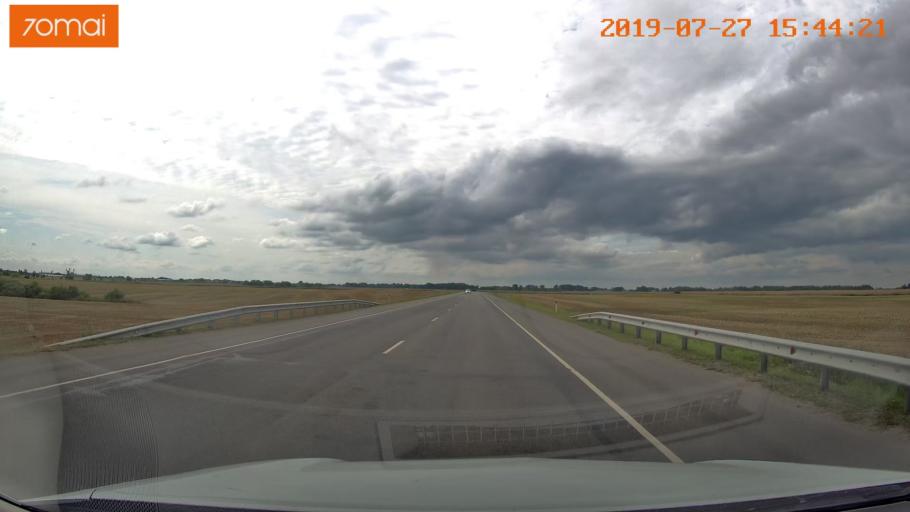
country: RU
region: Kaliningrad
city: Gusev
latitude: 54.6151
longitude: 22.1679
